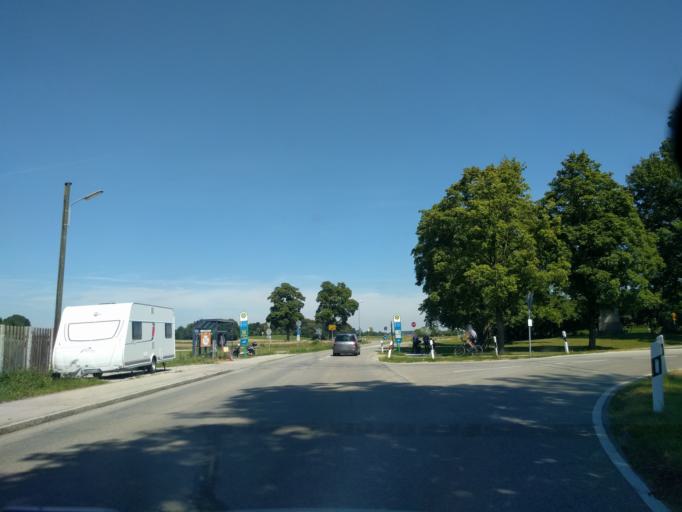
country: DE
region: Bavaria
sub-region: Upper Bavaria
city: Fuerstenfeldbruck
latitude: 48.1885
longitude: 11.2258
